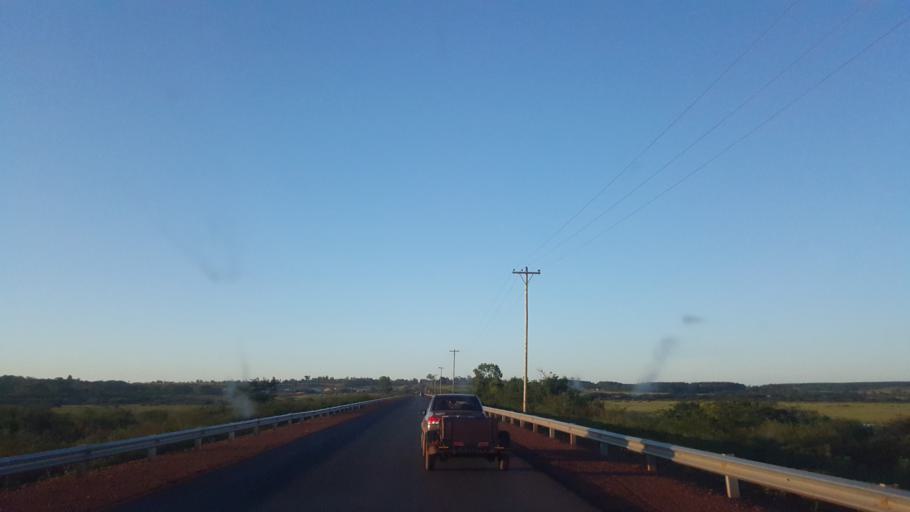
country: AR
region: Corrientes
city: Santo Tome
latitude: -28.5386
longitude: -56.0507
